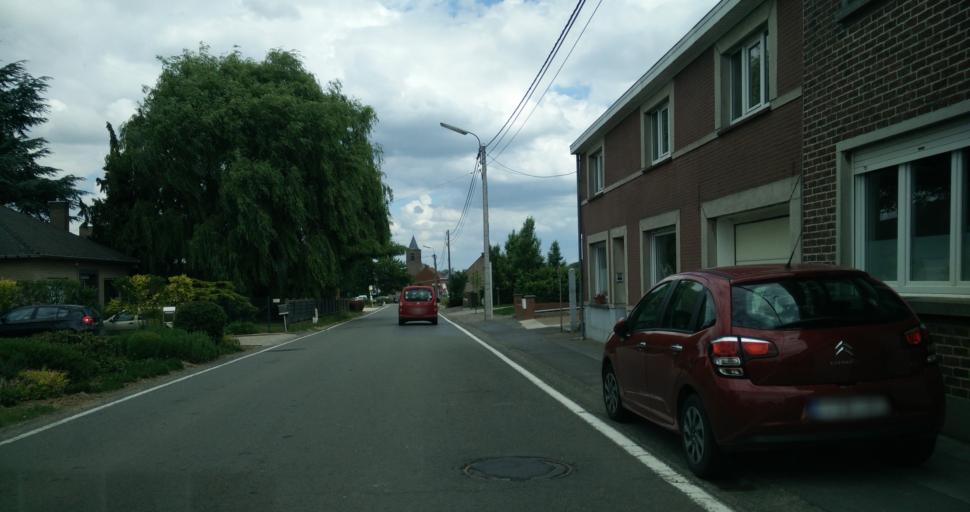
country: BE
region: Flanders
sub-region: Provincie Vlaams-Brabant
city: Galmaarden
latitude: 50.7141
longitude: 3.9349
